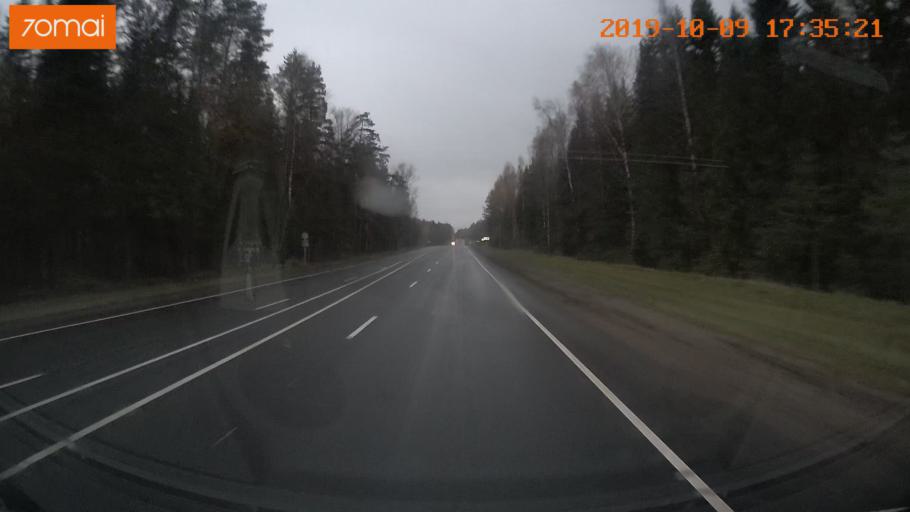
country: RU
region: Ivanovo
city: Bogorodskoye
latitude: 57.0949
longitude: 41.0027
